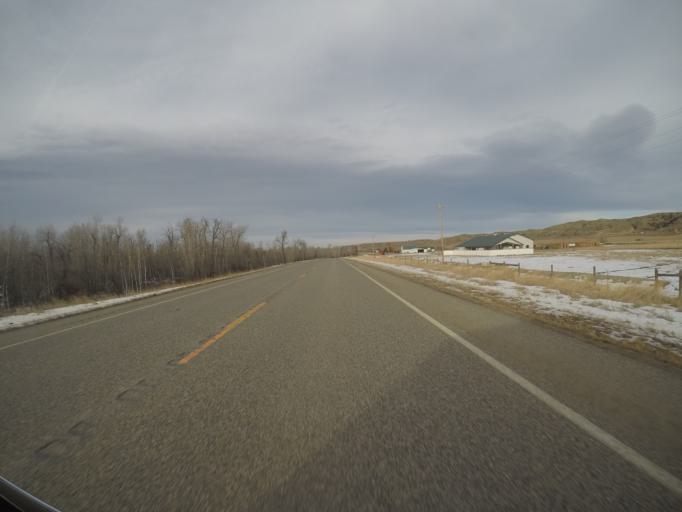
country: US
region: Montana
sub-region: Stillwater County
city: Absarokee
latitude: 45.4583
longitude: -109.4489
